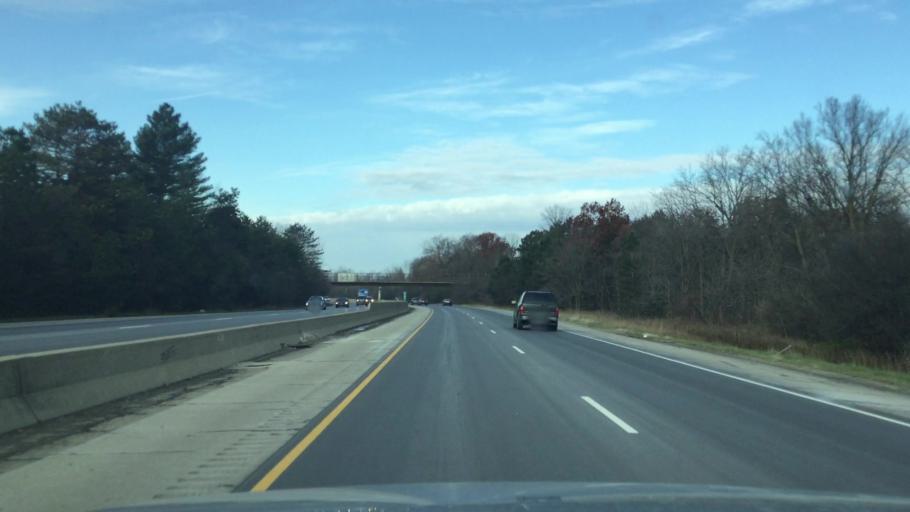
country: US
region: Michigan
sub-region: Washtenaw County
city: Ann Arbor
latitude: 42.2355
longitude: -83.7065
